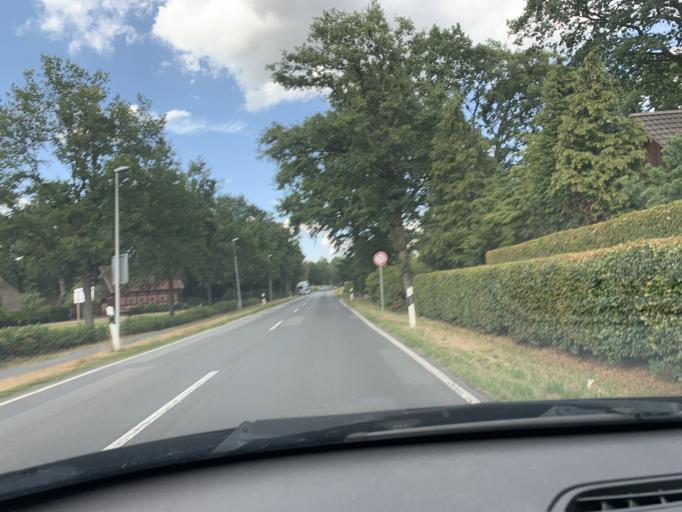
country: DE
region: Lower Saxony
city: Bad Zwischenahn
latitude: 53.1843
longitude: 8.0334
